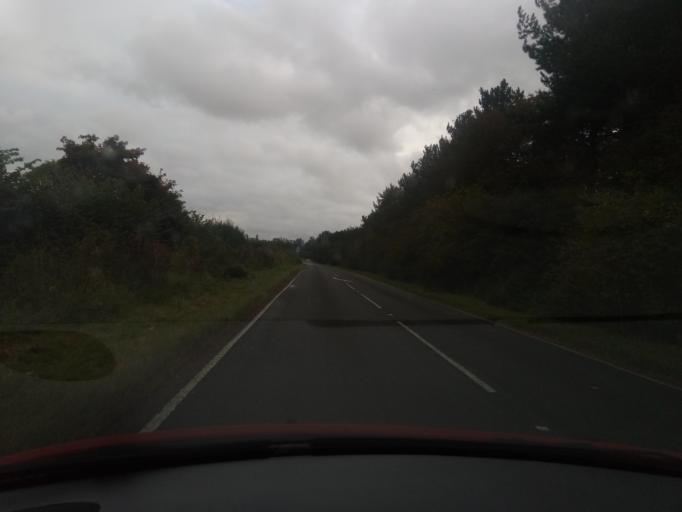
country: GB
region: England
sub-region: Nottinghamshire
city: Radcliffe on Trent
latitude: 52.9289
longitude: -1.0456
